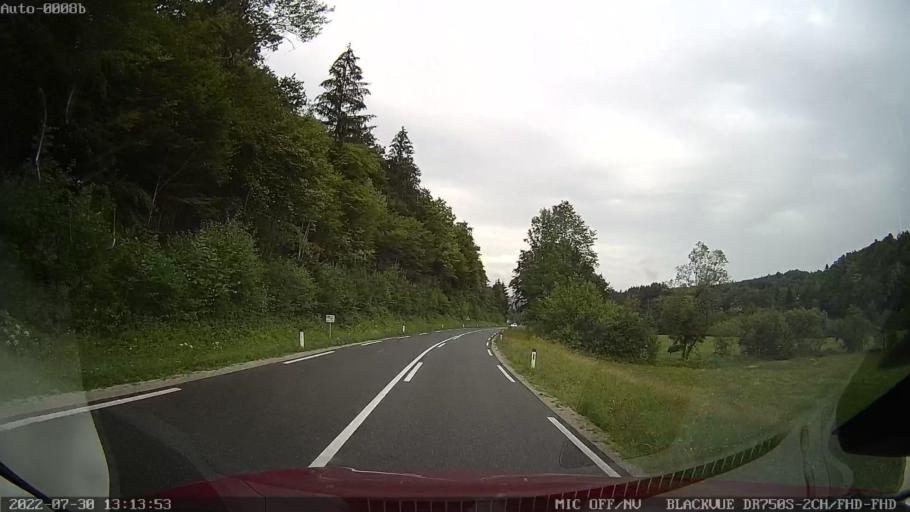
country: SI
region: Dolenjske Toplice
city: Dolenjske Toplice
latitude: 45.7249
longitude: 15.0525
